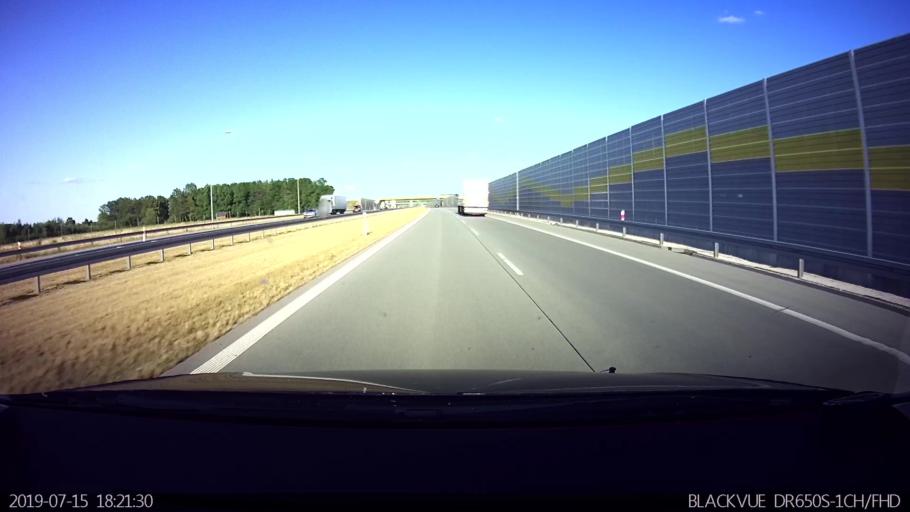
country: PL
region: Lodz Voivodeship
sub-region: Powiat laski
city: Lask
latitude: 51.5538
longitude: 19.0785
